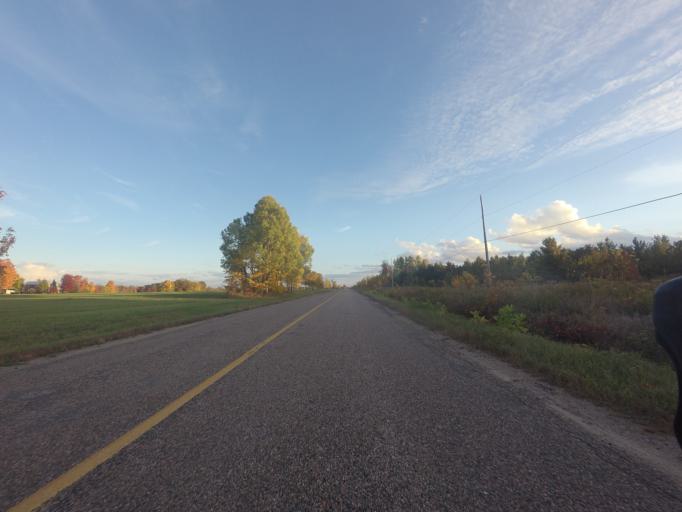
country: CA
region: Ontario
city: Renfrew
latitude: 45.4615
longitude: -76.9760
